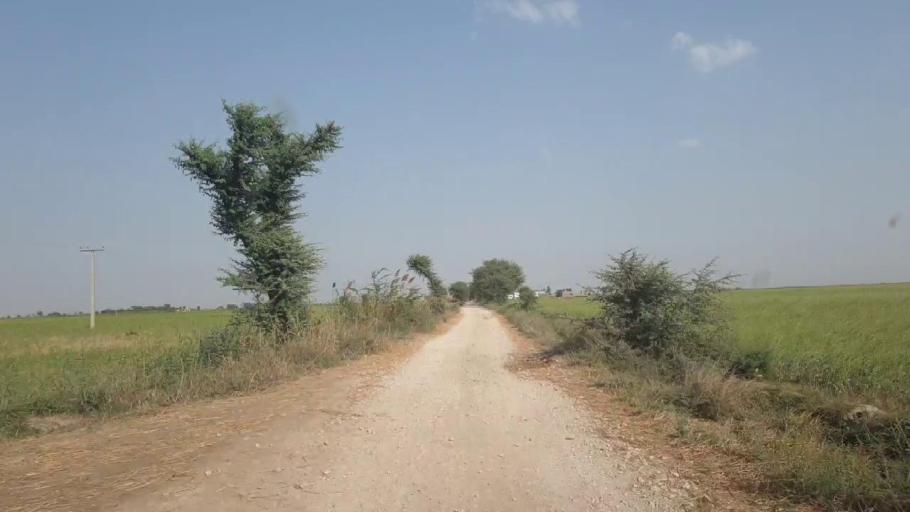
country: PK
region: Sindh
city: Kario
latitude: 24.5532
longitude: 68.5376
